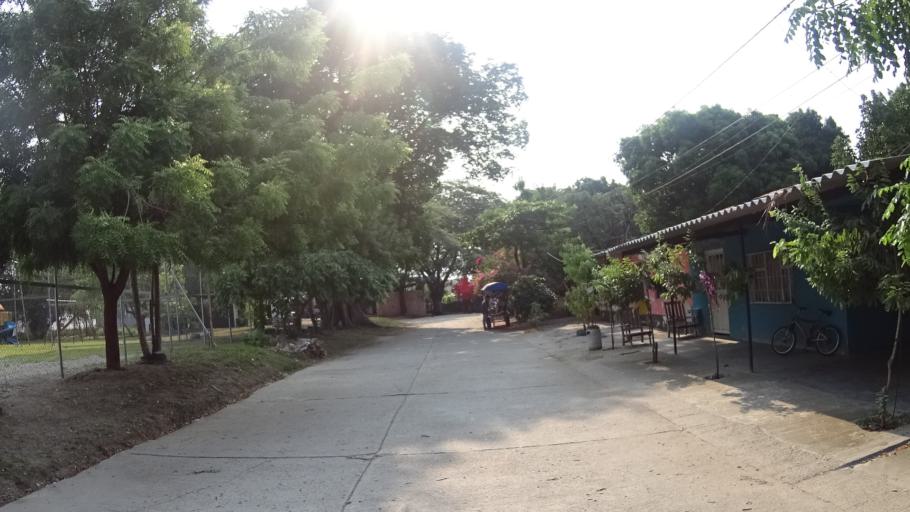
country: CO
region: Caldas
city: La Dorada
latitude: 5.4449
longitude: -74.6672
